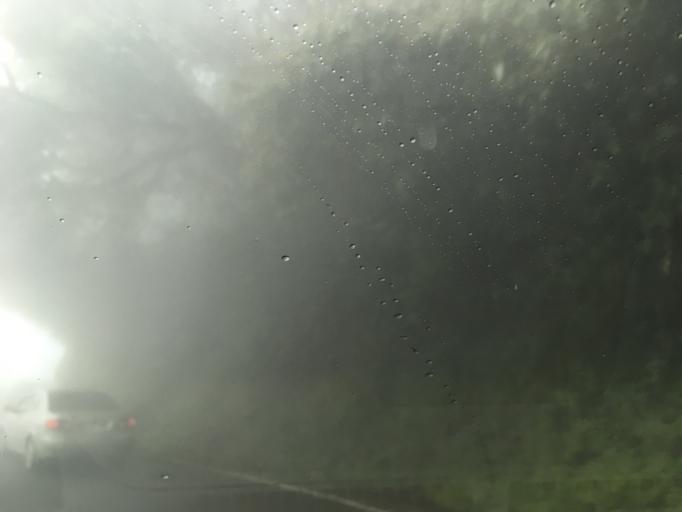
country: TW
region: Taiwan
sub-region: Hualien
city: Hualian
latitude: 24.1871
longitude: 121.4217
